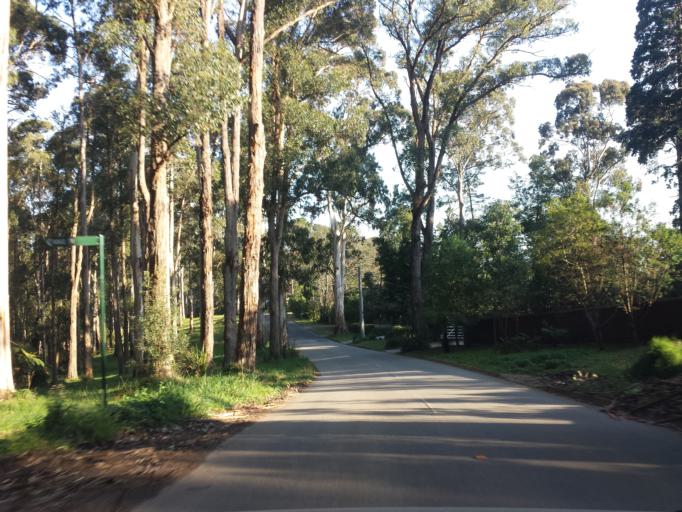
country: AU
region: Victoria
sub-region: Yarra Ranges
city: Belgrave
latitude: -37.8923
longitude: 145.3464
